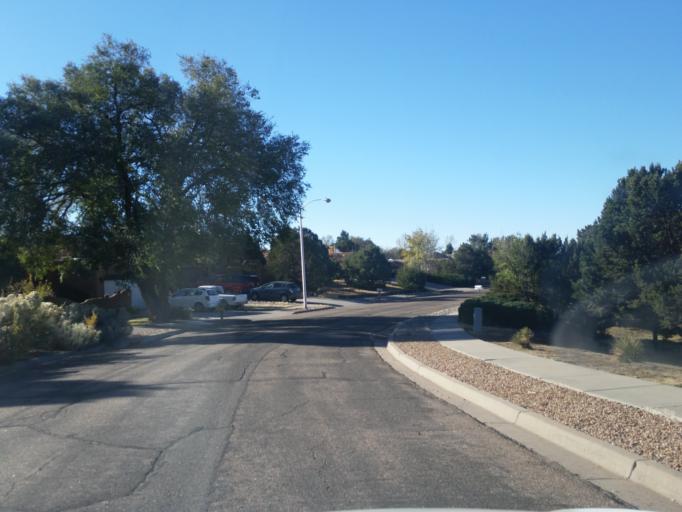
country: US
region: New Mexico
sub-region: Santa Fe County
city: Santa Fe
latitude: 35.6508
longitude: -105.9315
